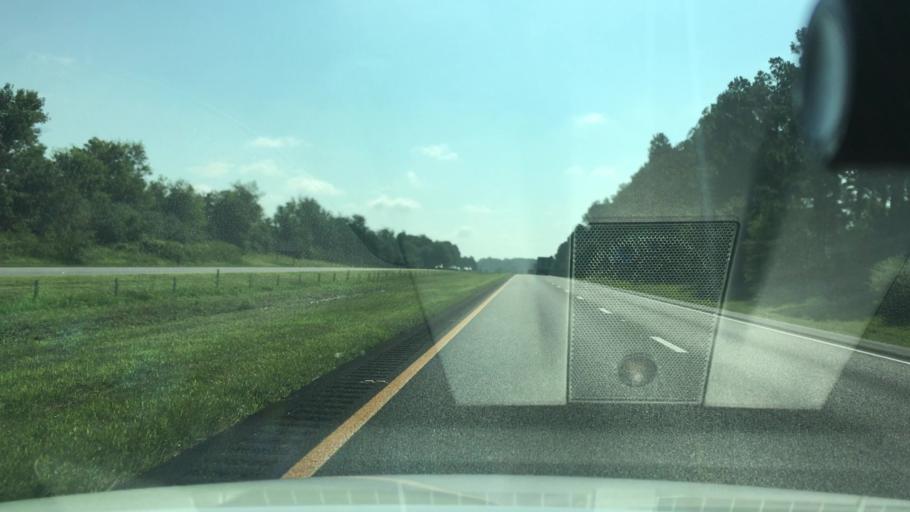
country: US
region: South Carolina
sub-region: Aiken County
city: Aiken
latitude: 33.6356
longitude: -81.7593
